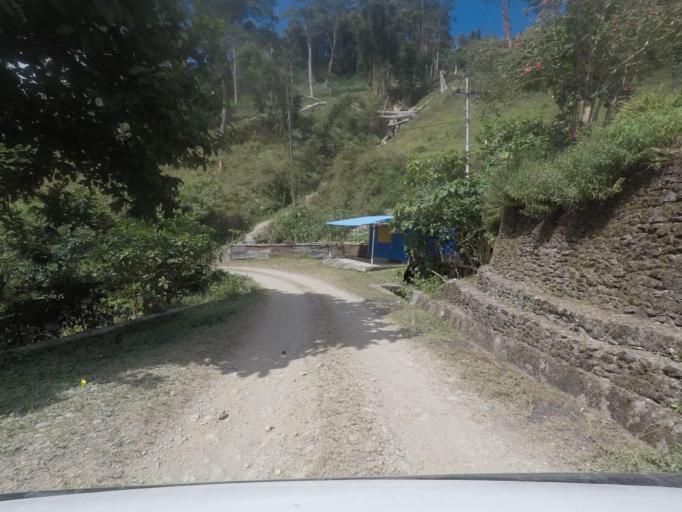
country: TL
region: Ermera
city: Gleno
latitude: -8.7513
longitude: 125.3254
